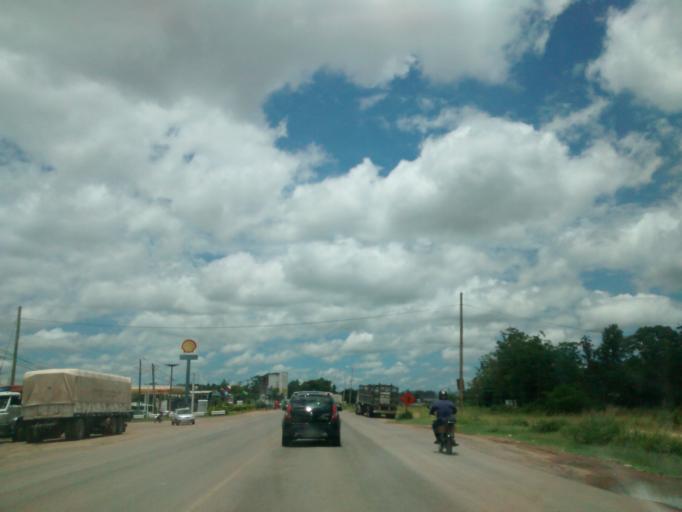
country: AR
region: Chaco
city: Fontana
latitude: -27.4149
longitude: -59.0033
